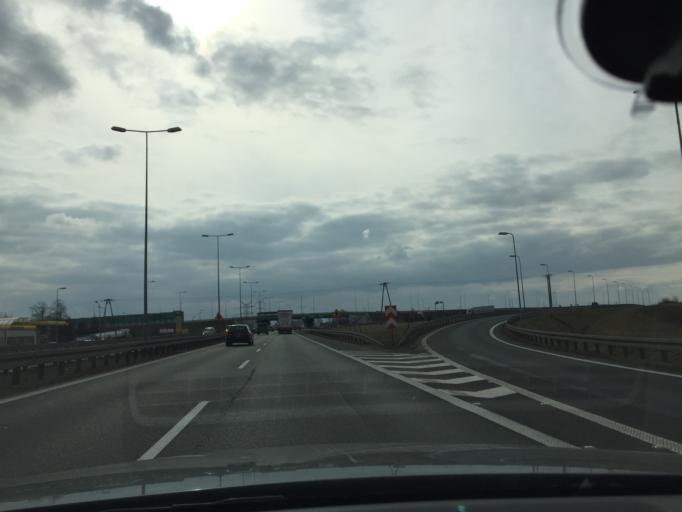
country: PL
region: Silesian Voivodeship
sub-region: Powiat bedzinski
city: Siewierz
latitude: 50.4629
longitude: 19.2310
